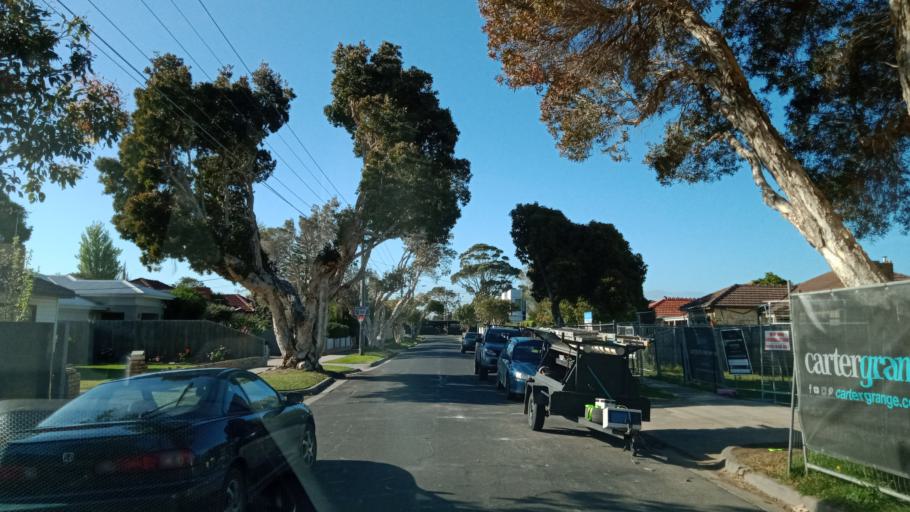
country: AU
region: Victoria
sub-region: Kingston
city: Edithvale
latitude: -38.0403
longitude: 145.1143
